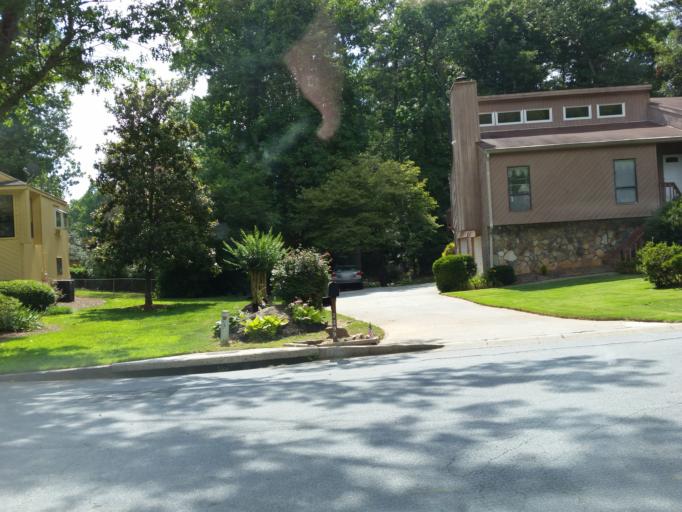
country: US
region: Georgia
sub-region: Cobb County
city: Marietta
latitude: 34.0052
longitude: -84.4751
